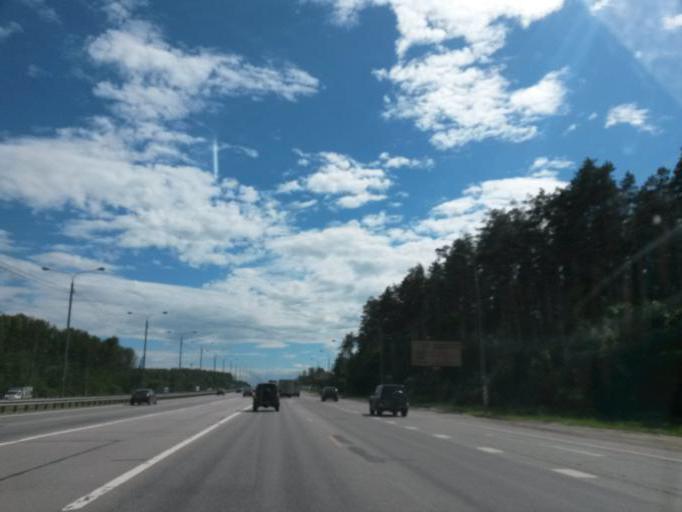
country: RU
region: Moskovskaya
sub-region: Podol'skiy Rayon
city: Podol'sk
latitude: 55.4238
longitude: 37.6115
